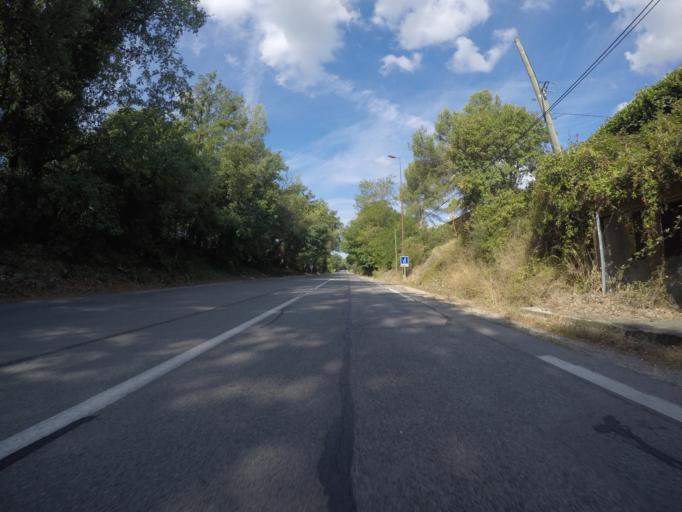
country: FR
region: Provence-Alpes-Cote d'Azur
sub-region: Departement des Alpes-Maritimes
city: Le Rouret
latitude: 43.6722
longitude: 7.0354
